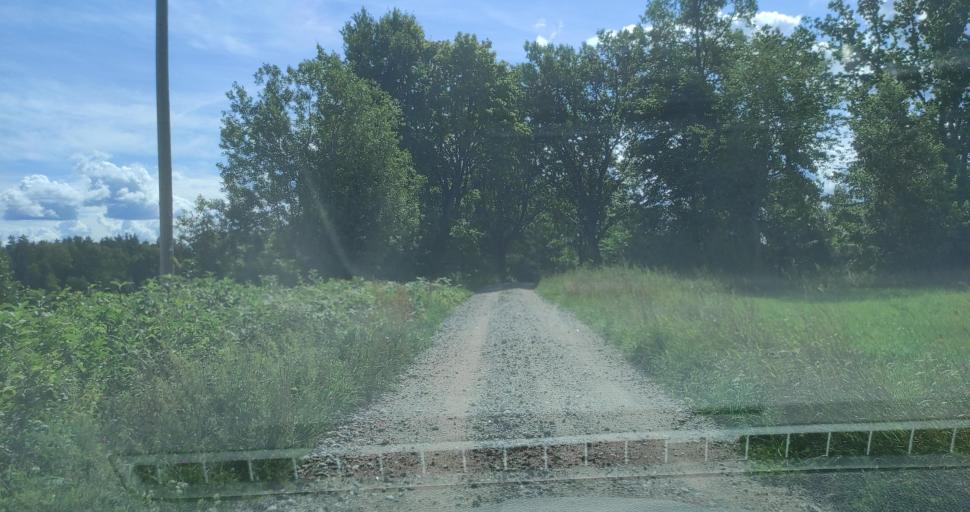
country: LV
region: Alsunga
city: Alsunga
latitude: 57.0305
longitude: 21.6976
